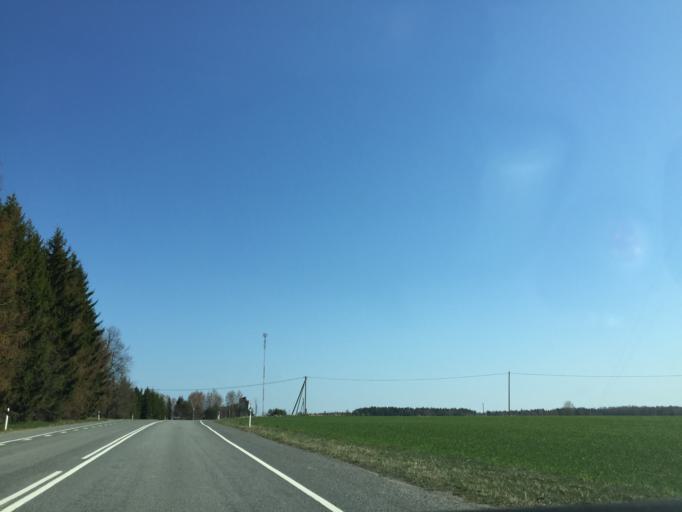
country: EE
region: Tartu
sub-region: Tartu linn
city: Tartu
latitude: 58.5081
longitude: 26.8876
